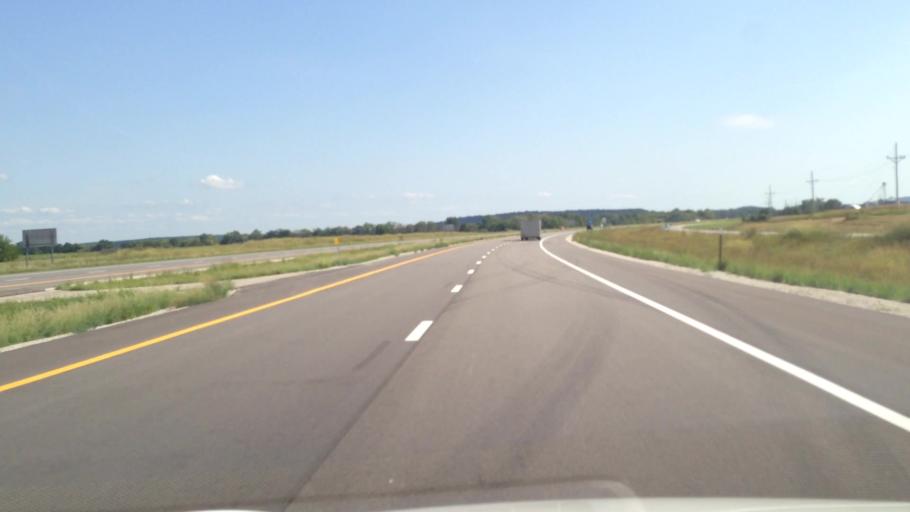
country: US
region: Kansas
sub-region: Linn County
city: La Cygne
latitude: 38.3376
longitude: -94.6792
